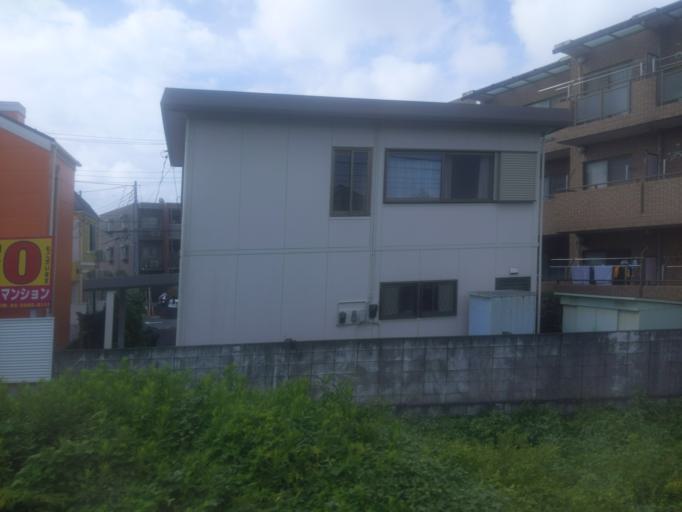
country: JP
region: Saitama
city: Wako
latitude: 35.7231
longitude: 139.6306
